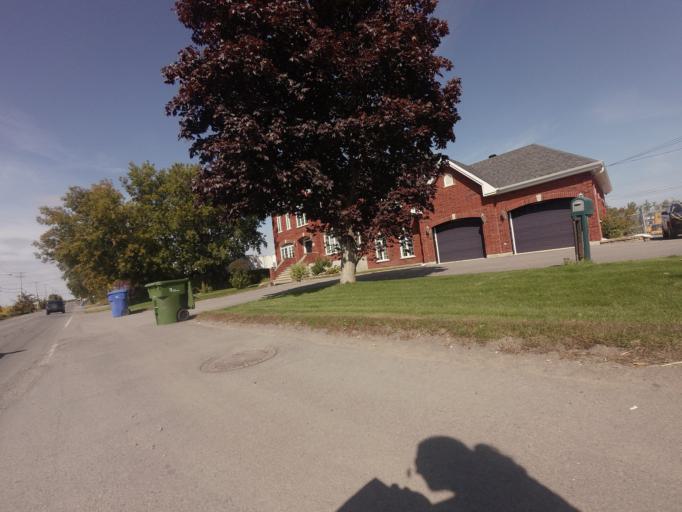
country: CA
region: Quebec
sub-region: Laurentides
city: Saint-Eustache
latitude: 45.5867
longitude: -73.9271
